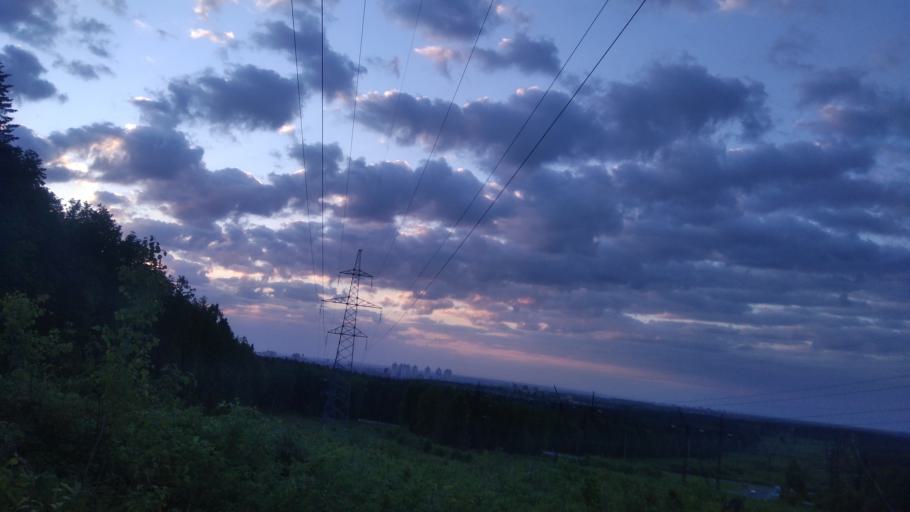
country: RU
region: Perm
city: Ferma
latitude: 57.9698
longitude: 56.3453
